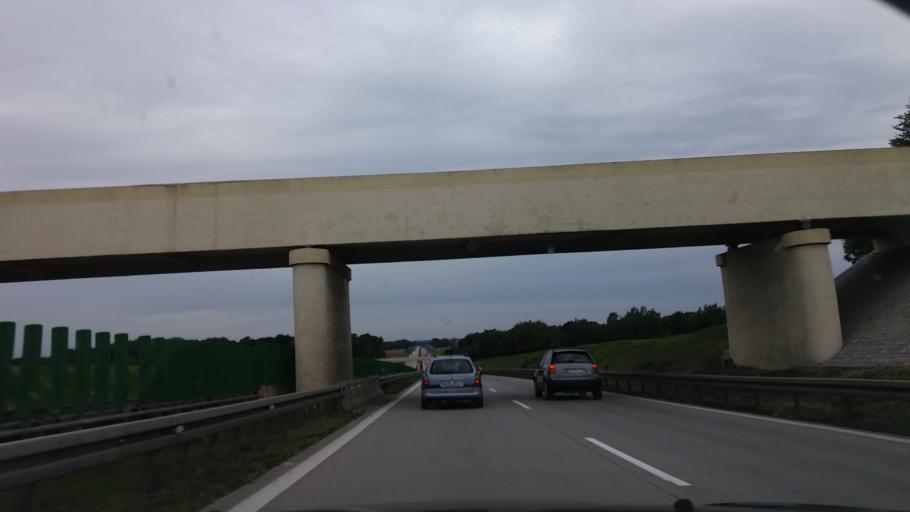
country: PL
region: Lower Silesian Voivodeship
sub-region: Powiat sredzki
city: Udanin
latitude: 51.0744
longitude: 16.4561
